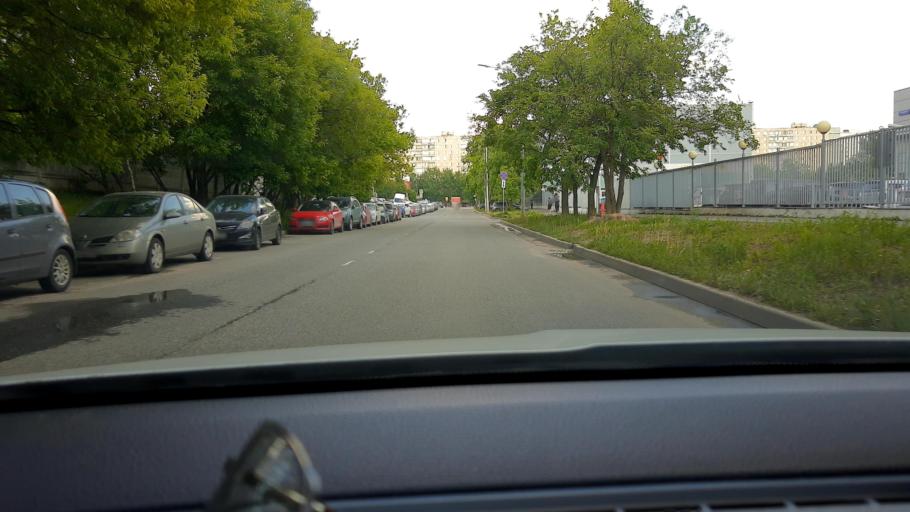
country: RU
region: Moscow
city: Slobodka
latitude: 55.8620
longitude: 37.5798
